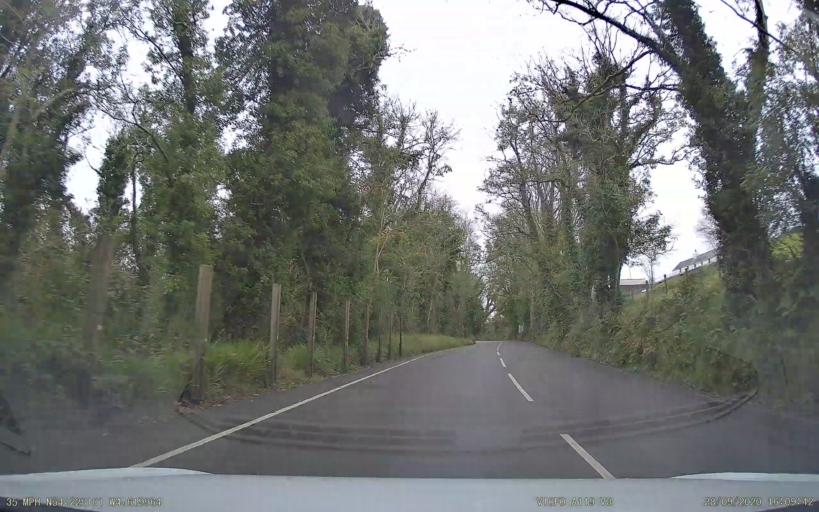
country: IM
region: Castletown
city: Castletown
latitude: 54.2281
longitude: -4.6200
